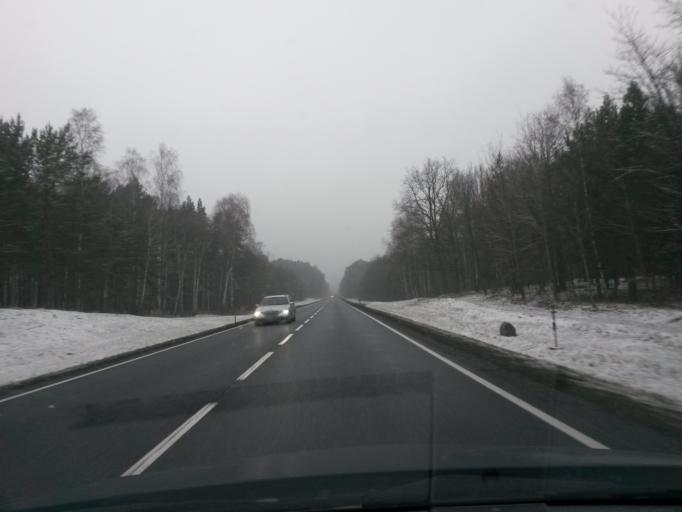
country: PL
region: Kujawsko-Pomorskie
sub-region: Powiat torunski
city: Wielka Nieszawka
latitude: 53.0044
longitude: 18.4468
